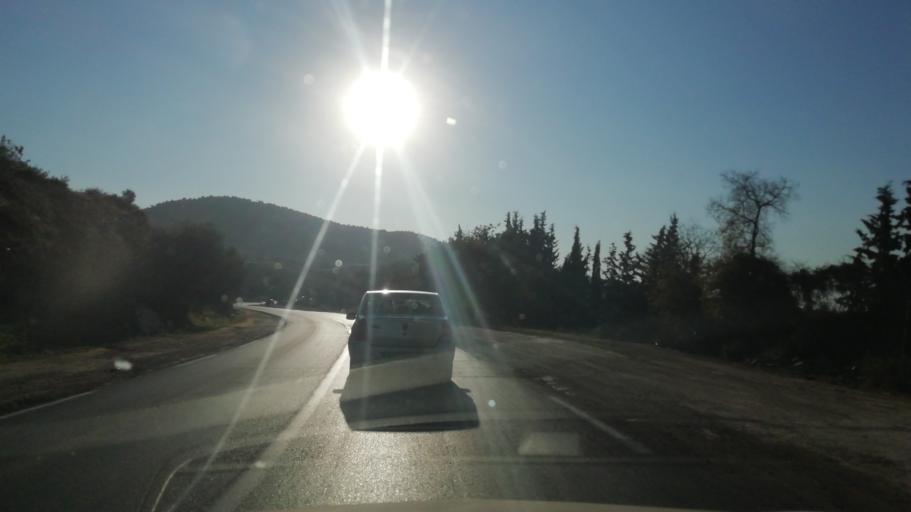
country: DZ
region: Tlemcen
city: Beni Mester
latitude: 34.8632
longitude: -1.4345
